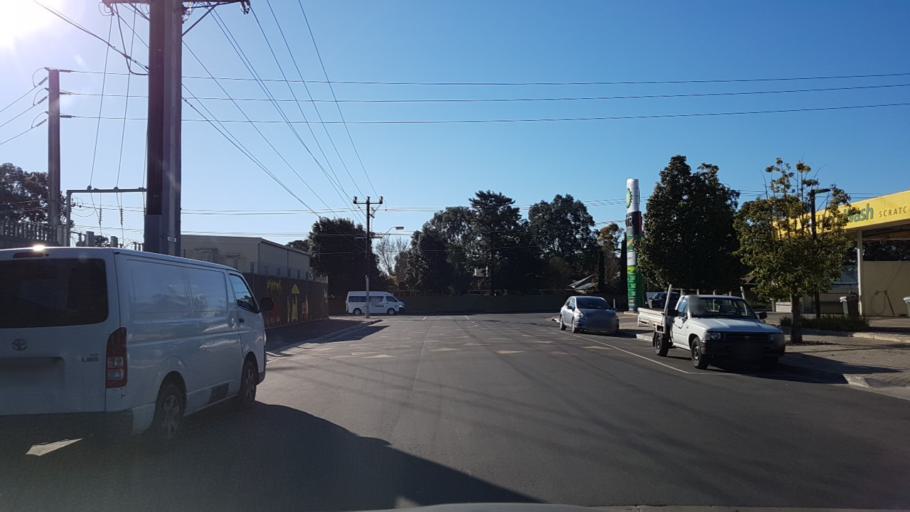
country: AU
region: South Australia
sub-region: Campbelltown
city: Paradise
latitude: -34.8769
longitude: 138.6734
